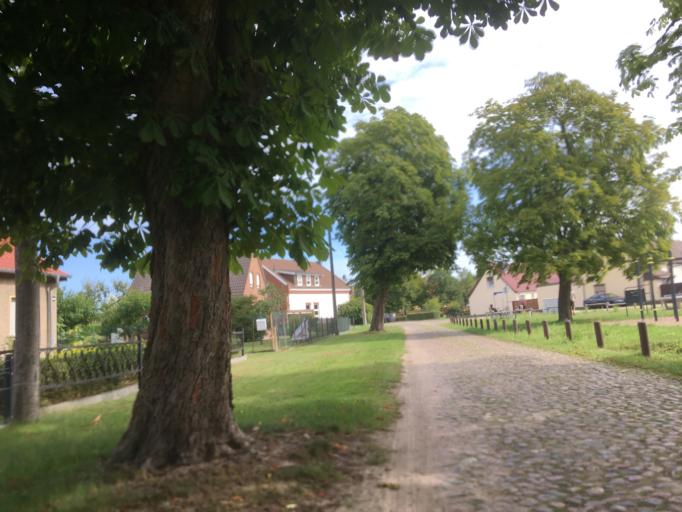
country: DE
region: Brandenburg
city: Wandlitz
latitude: 52.7515
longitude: 13.3708
